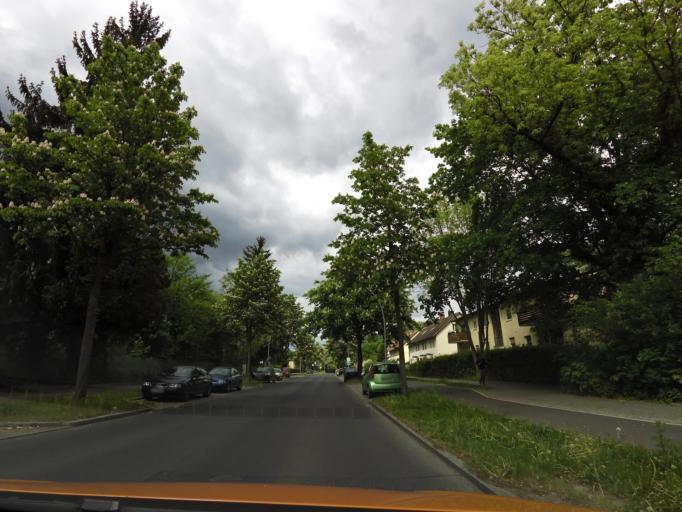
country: DE
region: Berlin
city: Zehlendorf Bezirk
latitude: 52.4241
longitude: 13.2518
